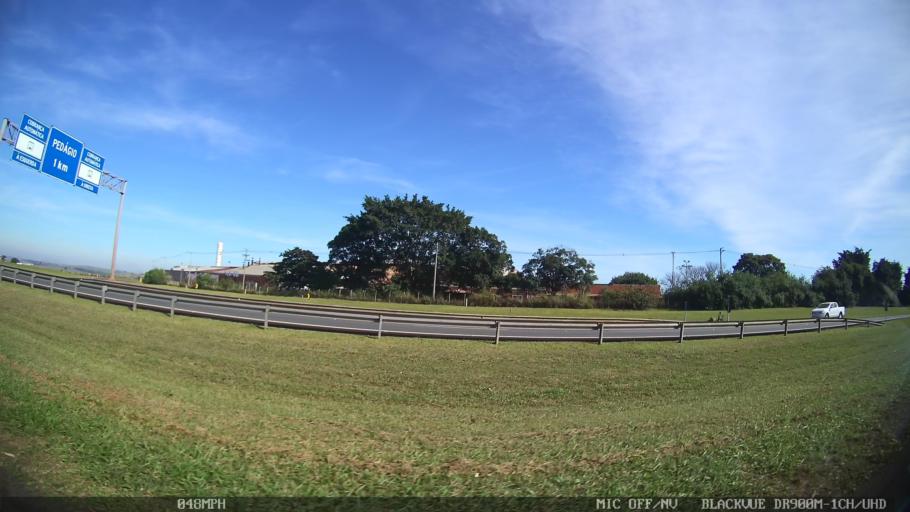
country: BR
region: Sao Paulo
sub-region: Cordeiropolis
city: Cordeiropolis
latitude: -22.4997
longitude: -47.3994
